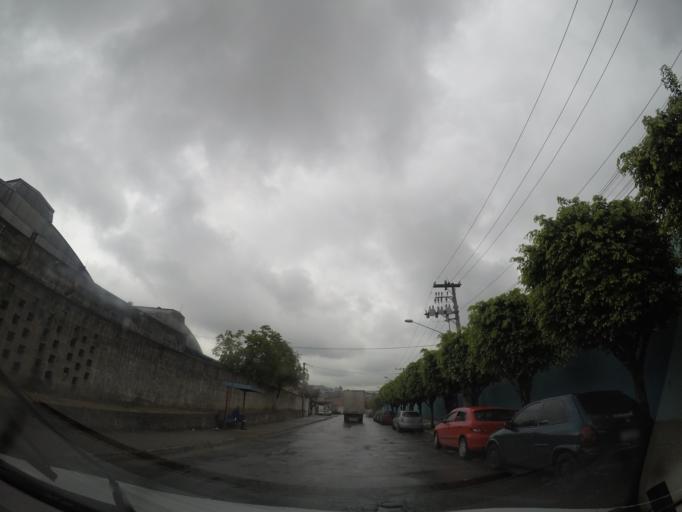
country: BR
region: Sao Paulo
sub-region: Guarulhos
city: Guarulhos
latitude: -23.4748
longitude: -46.4426
